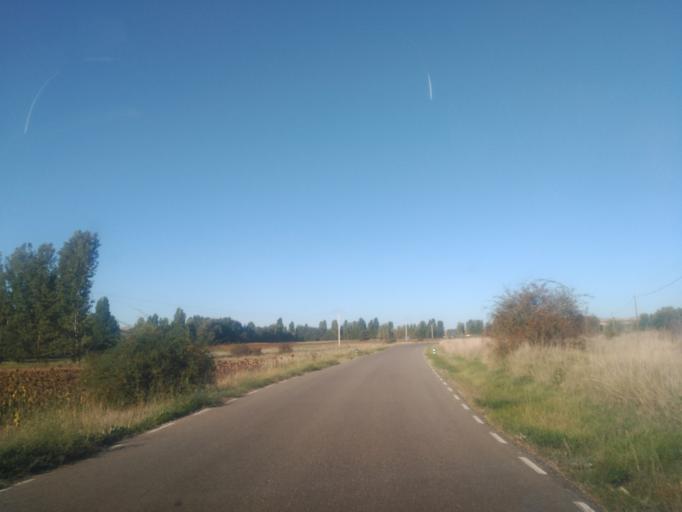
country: ES
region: Castille and Leon
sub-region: Provincia de Burgos
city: Penaranda de Duero
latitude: 41.6869
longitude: -3.4547
